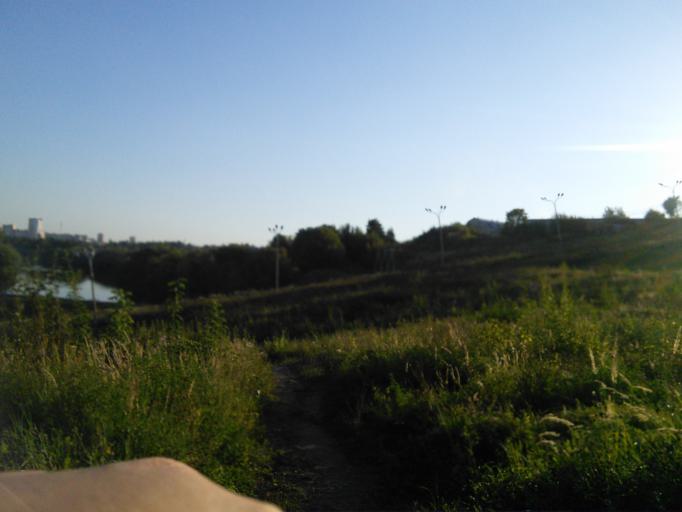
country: RU
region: Moskovskaya
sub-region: Podol'skiy Rayon
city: Podol'sk
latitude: 55.4490
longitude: 37.5614
